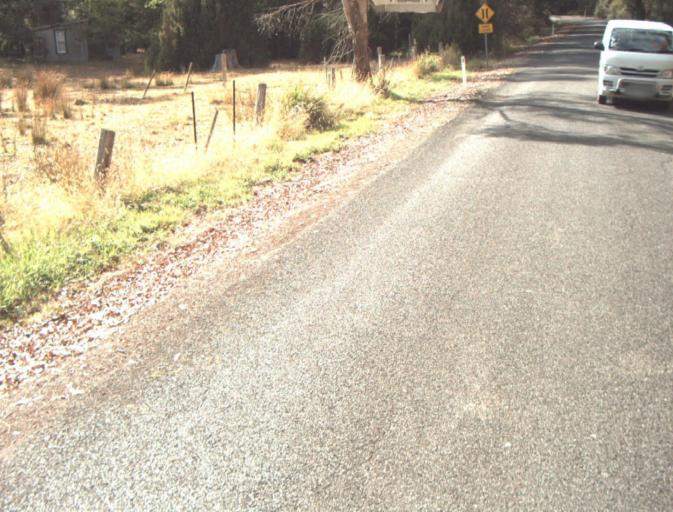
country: AU
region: Tasmania
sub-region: Launceston
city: Mayfield
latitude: -41.2697
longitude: 147.1628
